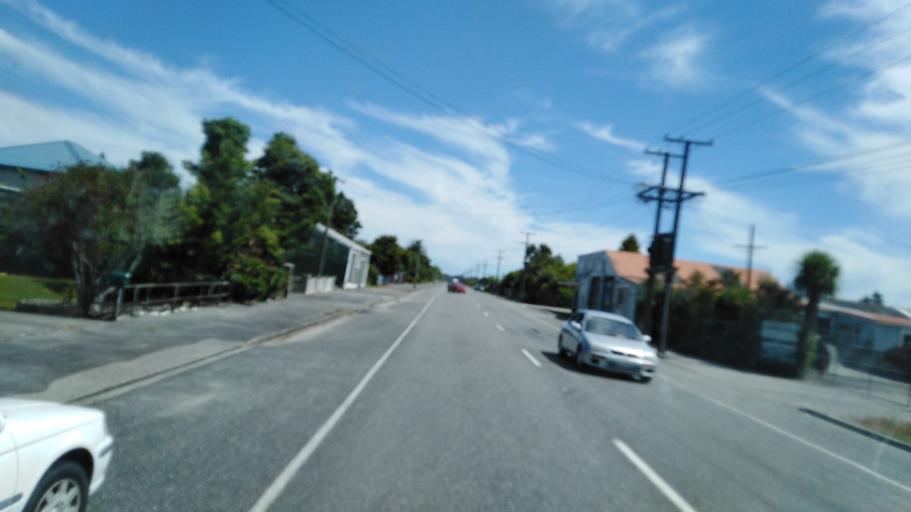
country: NZ
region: West Coast
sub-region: Buller District
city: Westport
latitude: -41.7526
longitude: 171.6211
